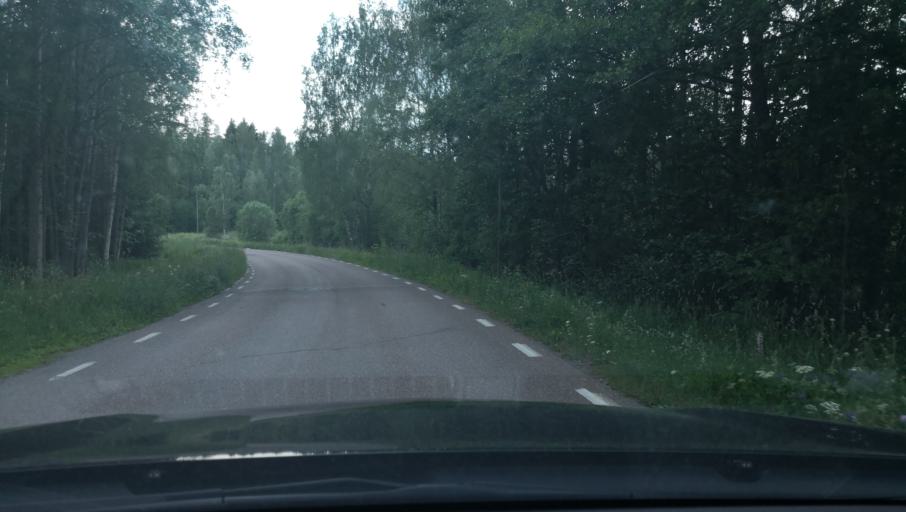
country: SE
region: Dalarna
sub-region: Smedjebackens Kommun
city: Smedjebacken
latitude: 60.0466
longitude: 15.5152
